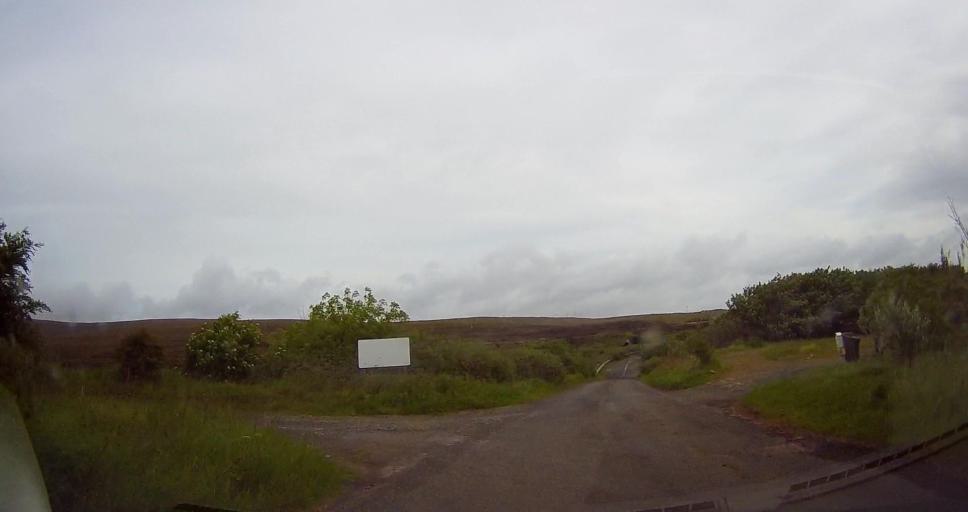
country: GB
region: Scotland
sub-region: Orkney Islands
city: Stromness
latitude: 58.8393
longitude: -3.2169
